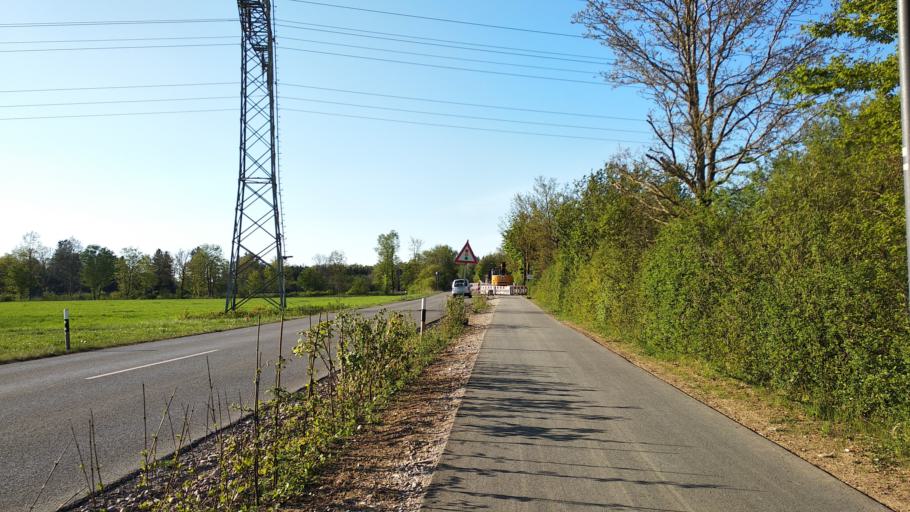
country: DE
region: Bavaria
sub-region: Upper Bavaria
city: Hohenbrunn
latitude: 48.0562
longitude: 11.6995
